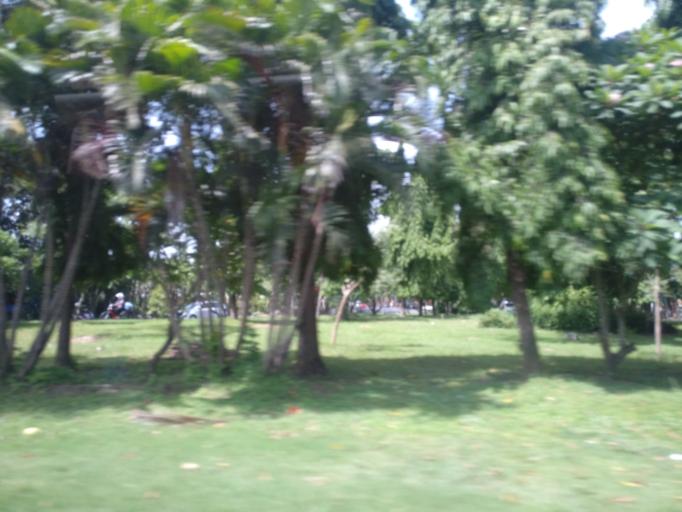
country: ID
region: Bali
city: Banjar Kertajiwa
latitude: -8.6495
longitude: 115.2575
